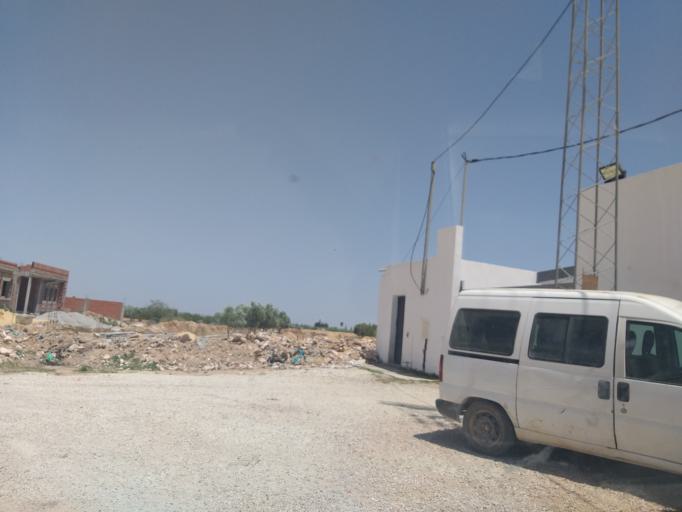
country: TN
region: Al Mahdiyah
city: El Jem
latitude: 35.3129
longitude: 10.7043
